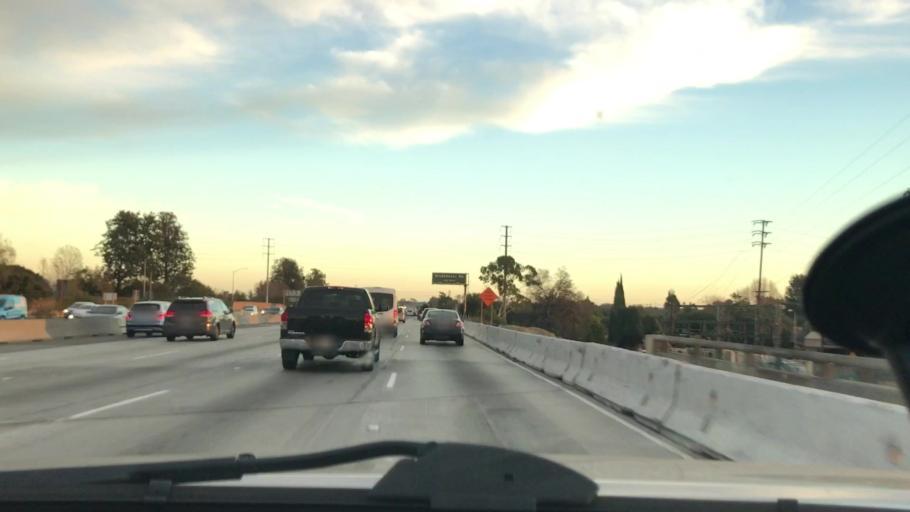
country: US
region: California
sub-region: Orange County
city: Rossmoor
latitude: 33.7967
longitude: -118.1082
